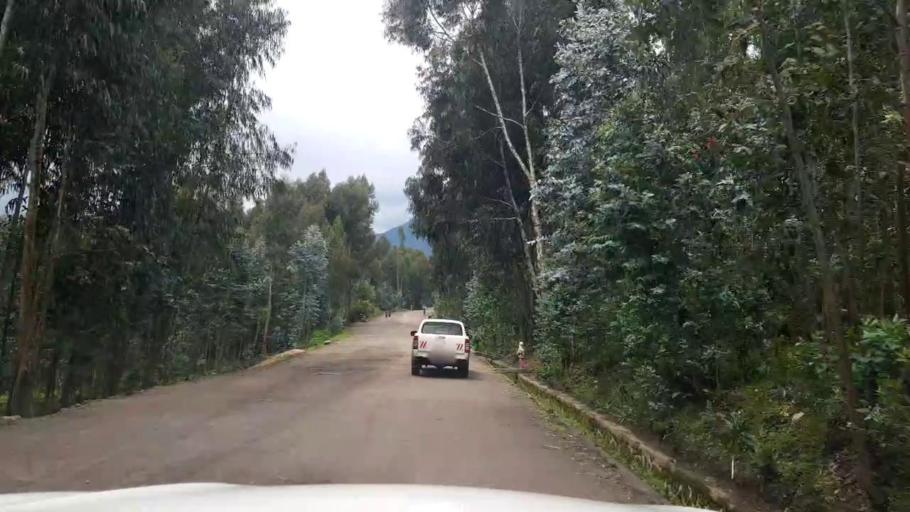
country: RW
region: Northern Province
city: Musanze
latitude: -1.4425
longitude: 29.5377
